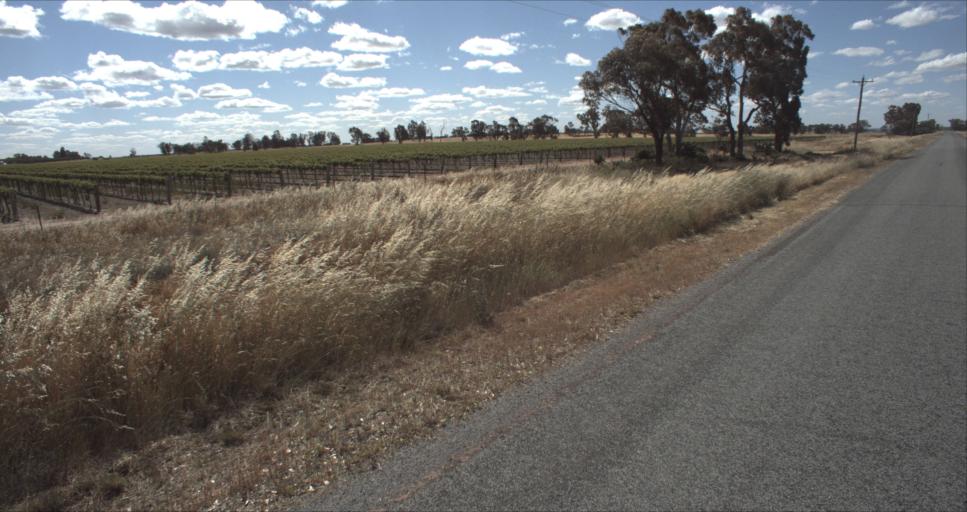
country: AU
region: New South Wales
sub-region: Leeton
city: Leeton
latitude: -34.4942
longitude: 146.2467
